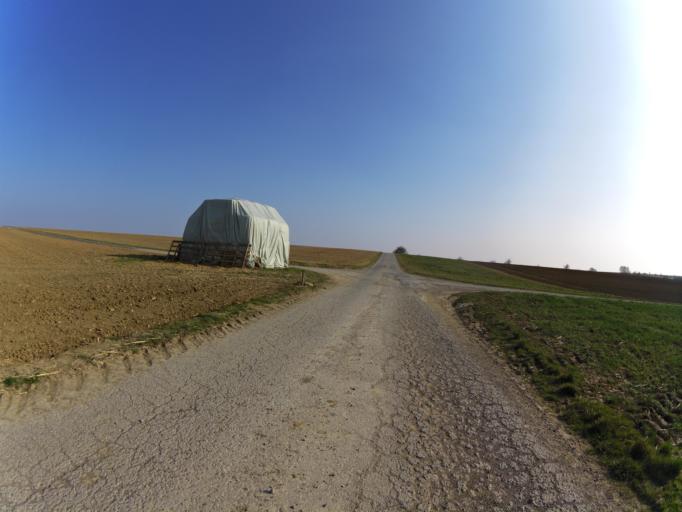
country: DE
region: Bavaria
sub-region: Regierungsbezirk Unterfranken
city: Eibelstadt
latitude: 49.6969
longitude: 9.9805
